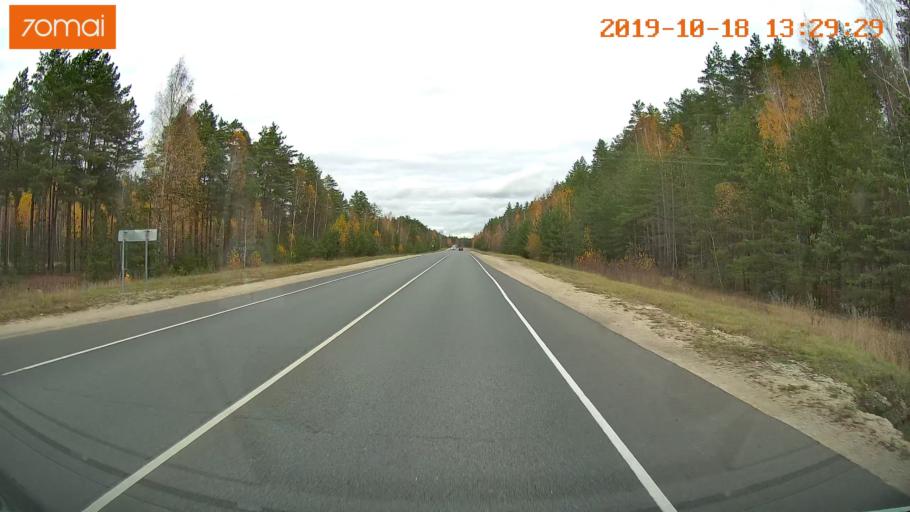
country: RU
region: Rjazan
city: Solotcha
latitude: 54.7953
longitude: 39.8752
